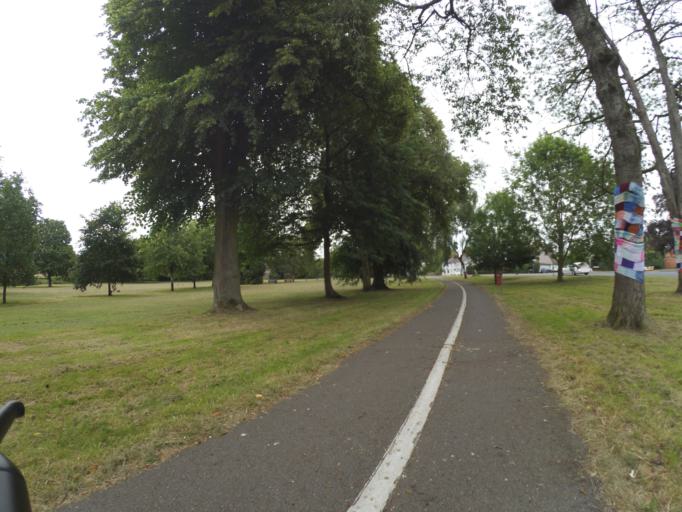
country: GB
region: England
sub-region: Warwickshire
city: Dunchurch
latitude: 52.3403
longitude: -1.2887
